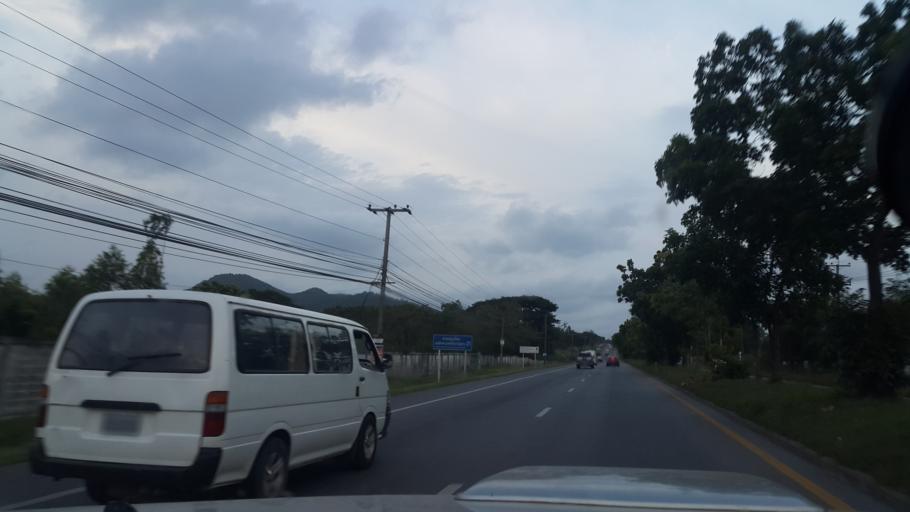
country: TH
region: Rayong
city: Ban Chang
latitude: 12.7038
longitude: 101.0132
